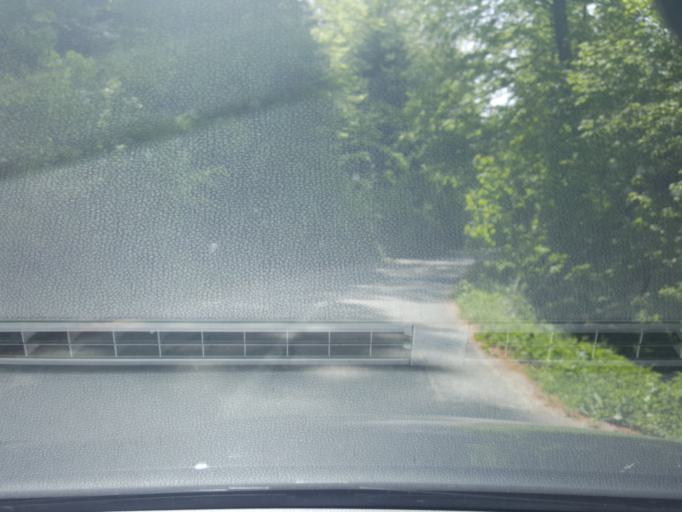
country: RS
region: Central Serbia
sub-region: Zlatiborski Okrug
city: Bajina Basta
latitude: 43.9127
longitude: 19.4956
